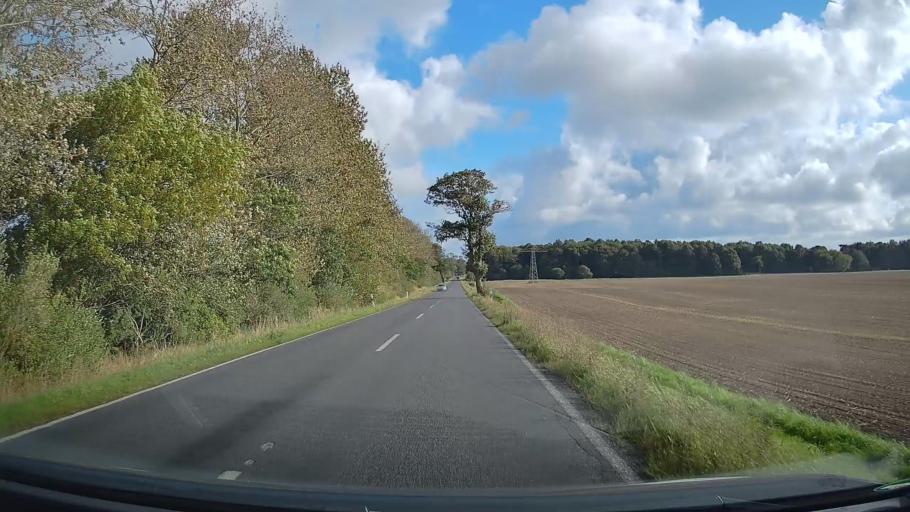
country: DE
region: Mecklenburg-Vorpommern
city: Bergen auf Ruegen
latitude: 54.4016
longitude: 13.4542
